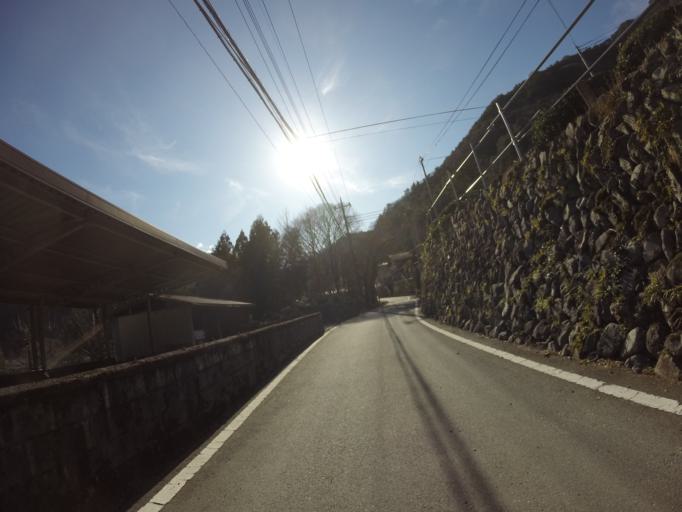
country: JP
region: Yamanashi
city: Ryuo
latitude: 35.3965
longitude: 138.3233
